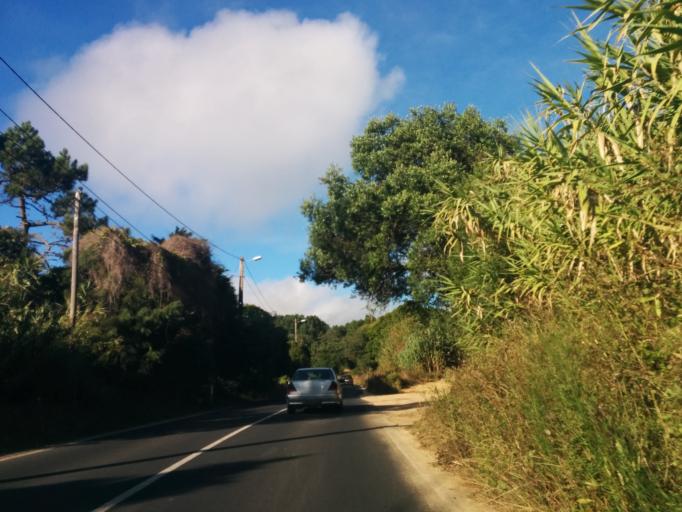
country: PT
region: Lisbon
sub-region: Sintra
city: Colares
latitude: 38.7804
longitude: -9.4747
